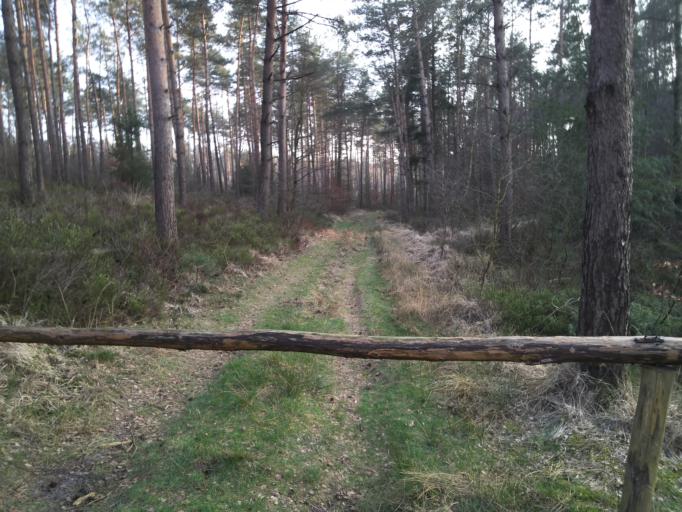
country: NL
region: Gelderland
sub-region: Gemeente Nunspeet
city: Nunspeet
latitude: 52.3265
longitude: 5.8545
